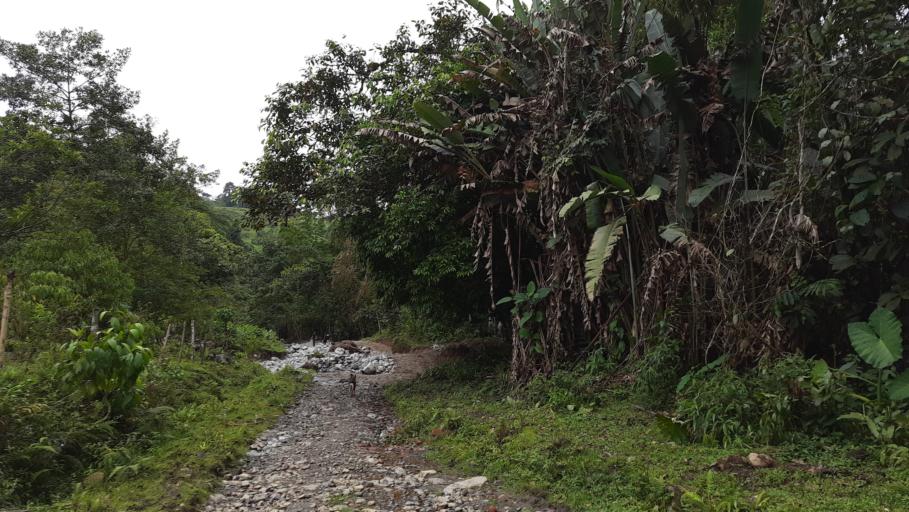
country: CO
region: Valle del Cauca
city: Buga
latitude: 3.8538
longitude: -76.1866
